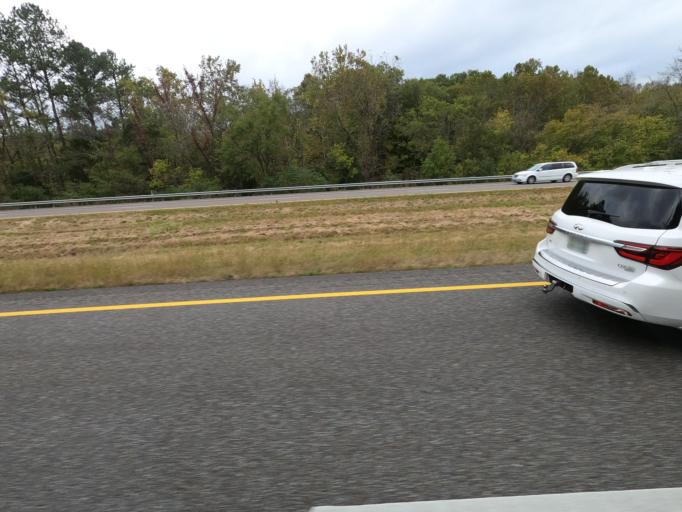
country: US
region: Tennessee
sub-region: Hickman County
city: Centerville
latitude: 35.8902
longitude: -87.6512
